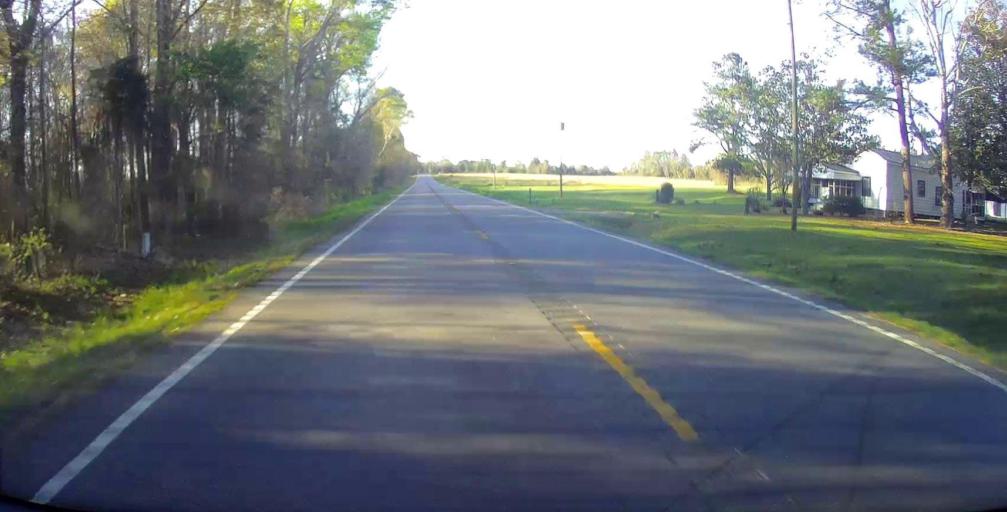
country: US
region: Georgia
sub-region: Pulaski County
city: Hawkinsville
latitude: 32.2280
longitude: -83.3936
